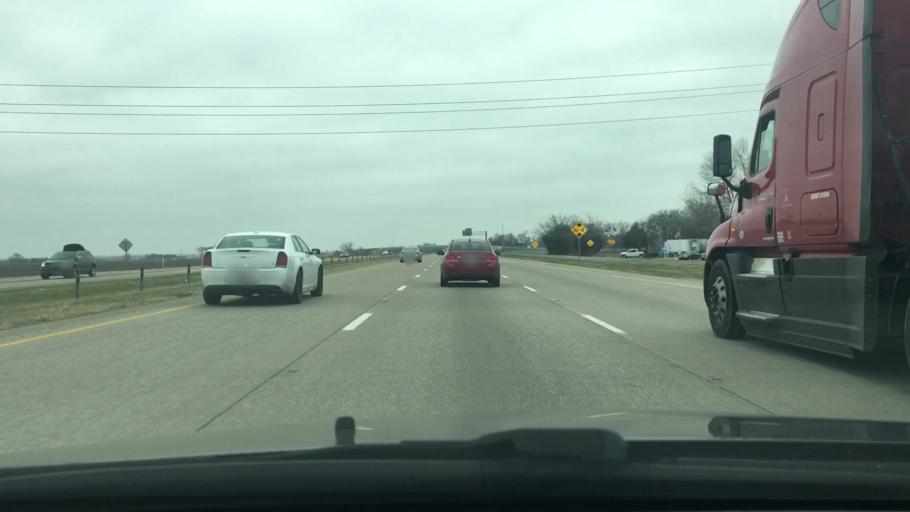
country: US
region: Texas
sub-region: Ellis County
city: Ferris
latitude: 32.4921
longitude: -96.6641
